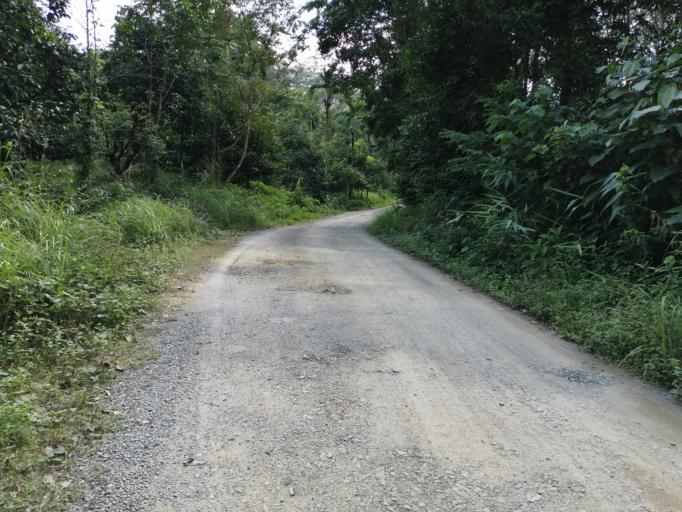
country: TH
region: Phatthalung
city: Pa Phayom
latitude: 7.9244
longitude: 99.8104
